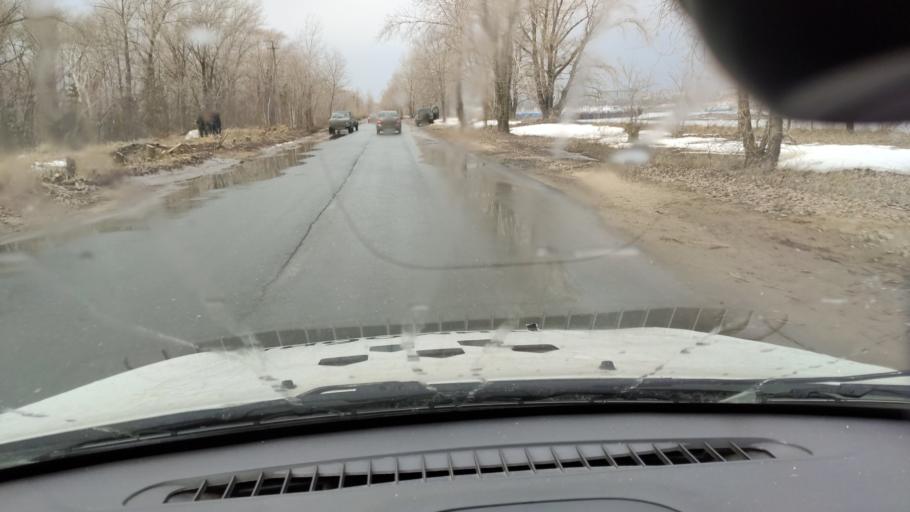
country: RU
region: Samara
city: Zhigulevsk
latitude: 53.4590
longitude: 49.5283
